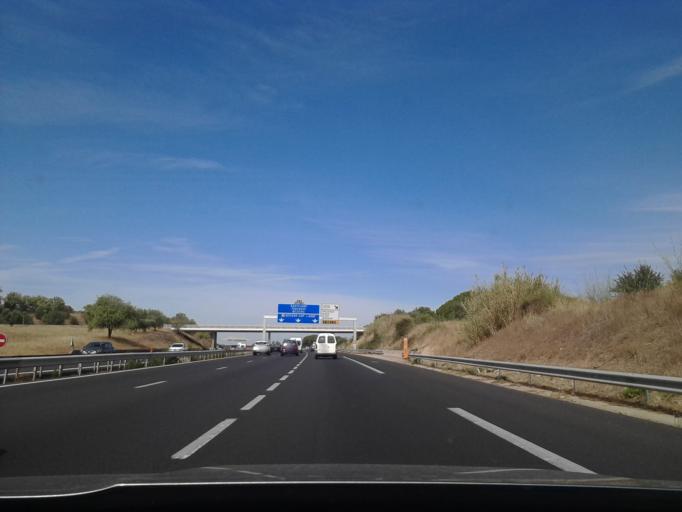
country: FR
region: Languedoc-Roussillon
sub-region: Departement de l'Herault
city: Bessan
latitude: 43.3769
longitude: 3.4182
